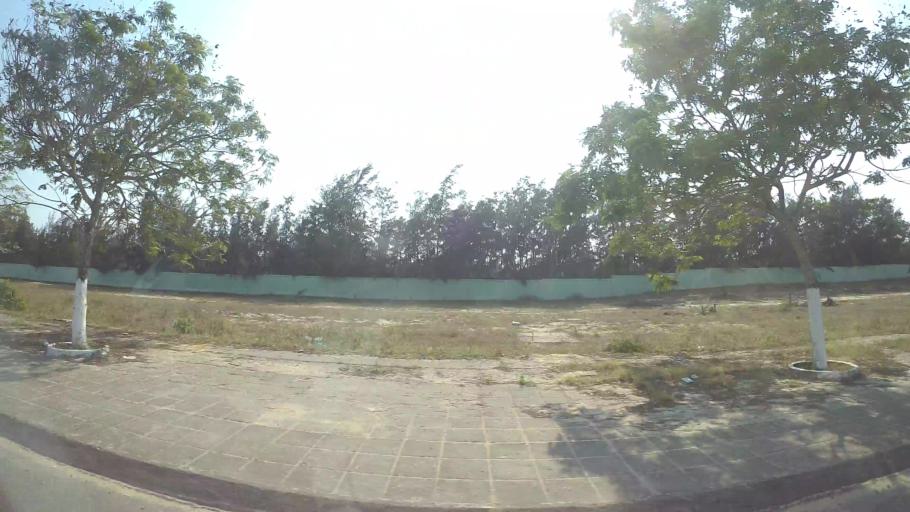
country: VN
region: Da Nang
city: Ngu Hanh Son
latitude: 15.9622
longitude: 108.2882
